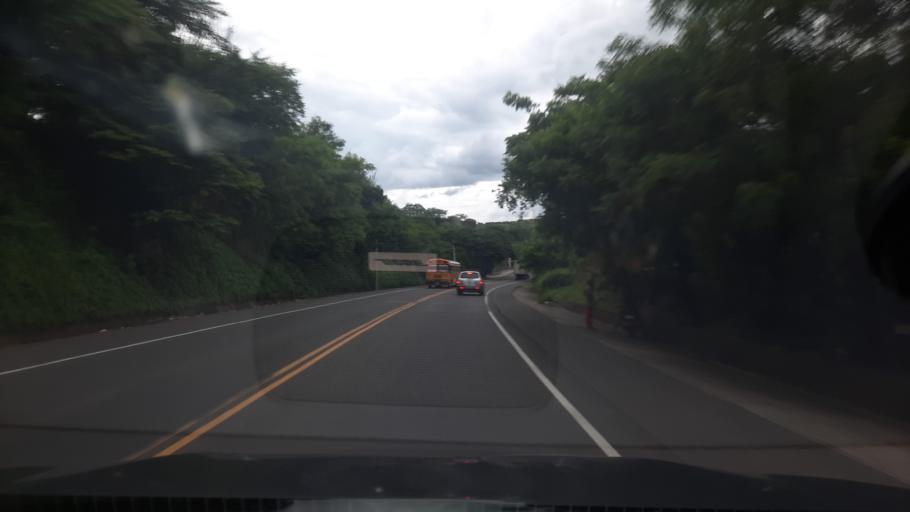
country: HN
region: Choluteca
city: Marcovia
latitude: 13.3519
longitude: -87.2631
